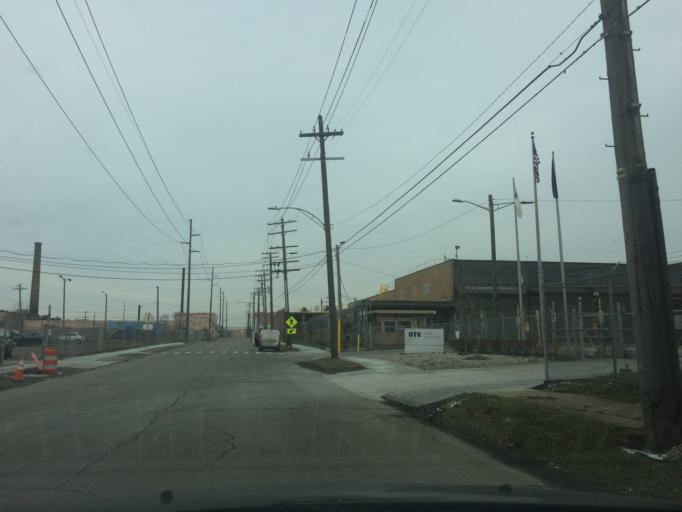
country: US
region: Michigan
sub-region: Wayne County
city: Hamtramck
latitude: 42.3735
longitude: -83.0562
